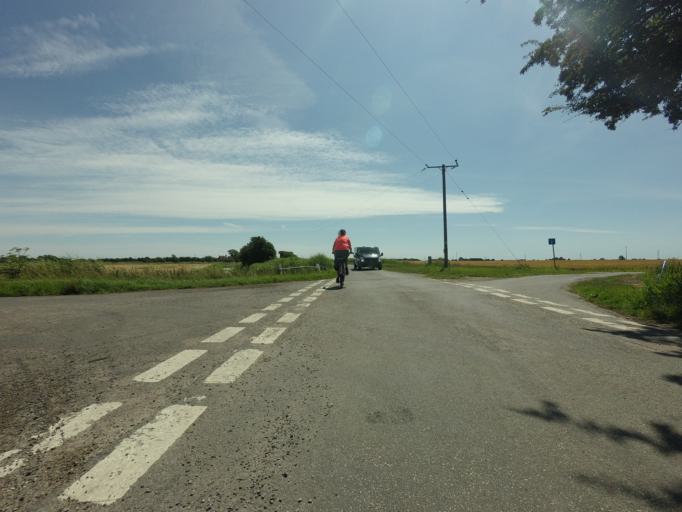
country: GB
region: England
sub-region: Kent
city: Lydd
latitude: 50.9793
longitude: 0.8470
